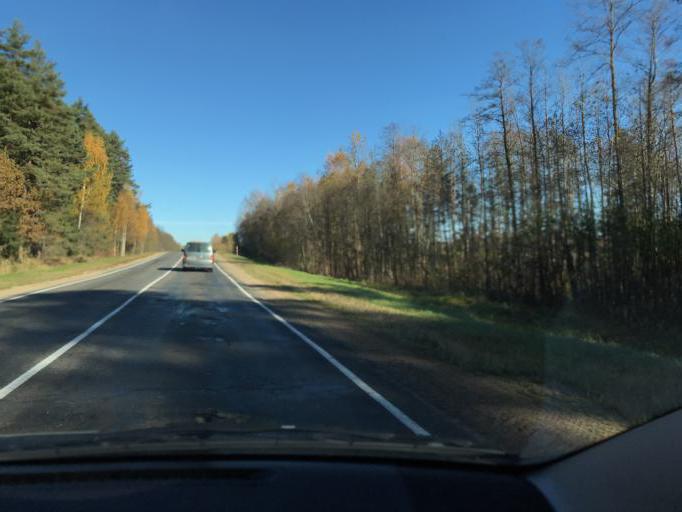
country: BY
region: Vitebsk
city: Polatsk
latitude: 55.3227
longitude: 28.7813
